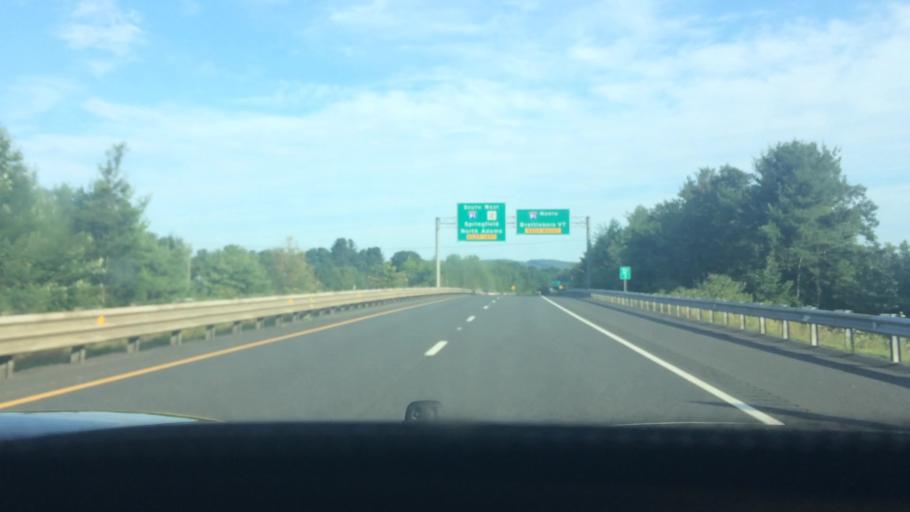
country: US
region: Massachusetts
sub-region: Franklin County
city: Greenfield
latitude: 42.6099
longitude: -72.5835
